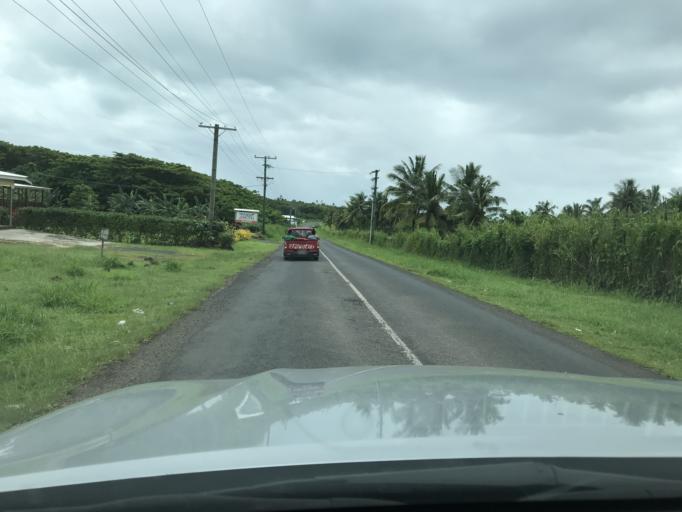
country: WS
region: Aiga-i-le-Tai
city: Mulifanua
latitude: -13.8327
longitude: -172.0263
